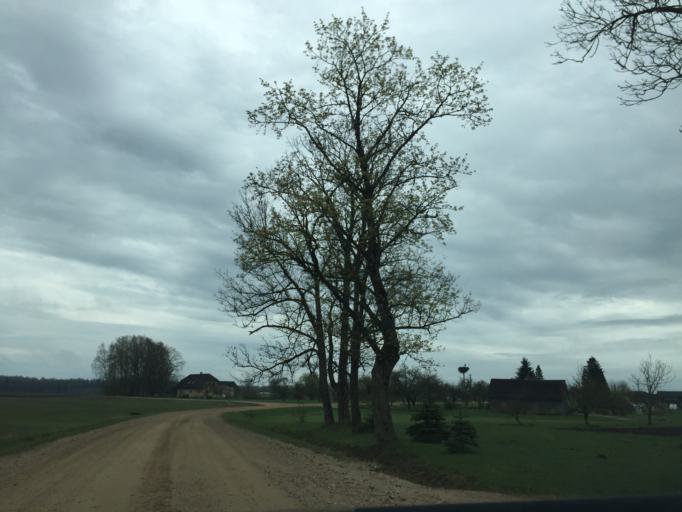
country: LV
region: Sigulda
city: Sigulda
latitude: 57.0427
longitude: 24.8431
